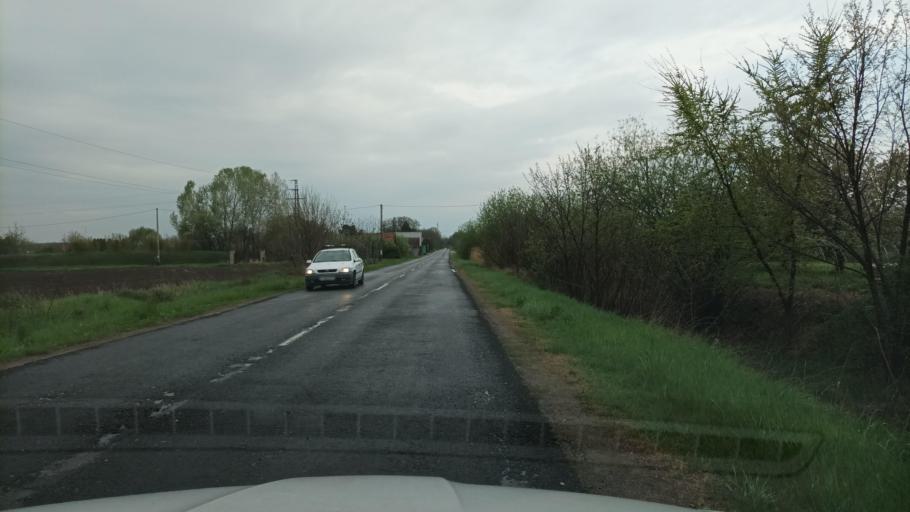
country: HU
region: Pest
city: Albertirsa
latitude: 47.2392
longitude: 19.5932
